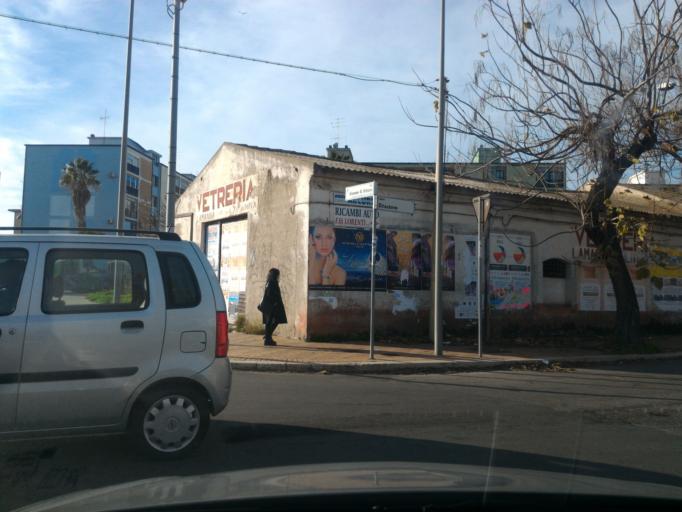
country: IT
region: Calabria
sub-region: Provincia di Crotone
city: Crotone
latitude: 39.0832
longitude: 17.1142
